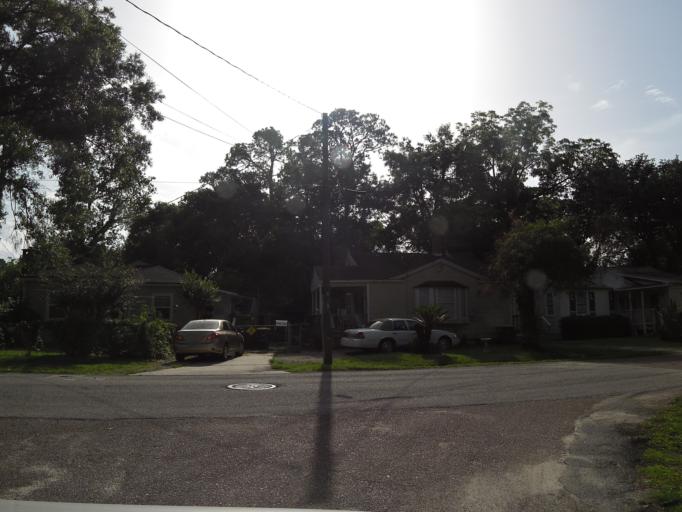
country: US
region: Florida
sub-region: Duval County
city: Jacksonville
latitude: 30.3040
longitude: -81.7262
